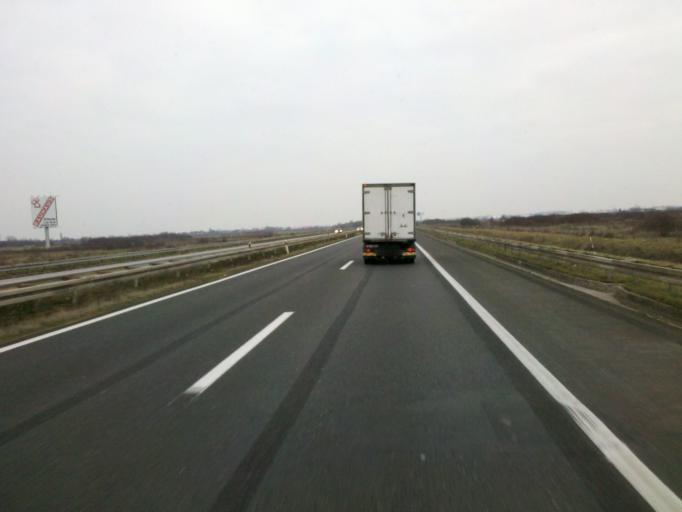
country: HR
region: Grad Zagreb
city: Odra
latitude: 45.7480
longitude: 16.0263
